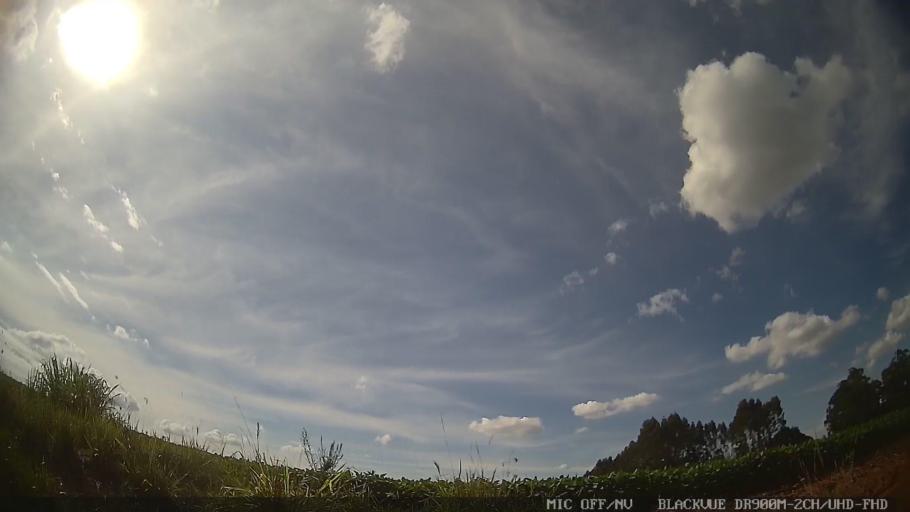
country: BR
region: Sao Paulo
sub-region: Cosmopolis
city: Cosmopolis
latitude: -22.6422
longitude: -47.0916
